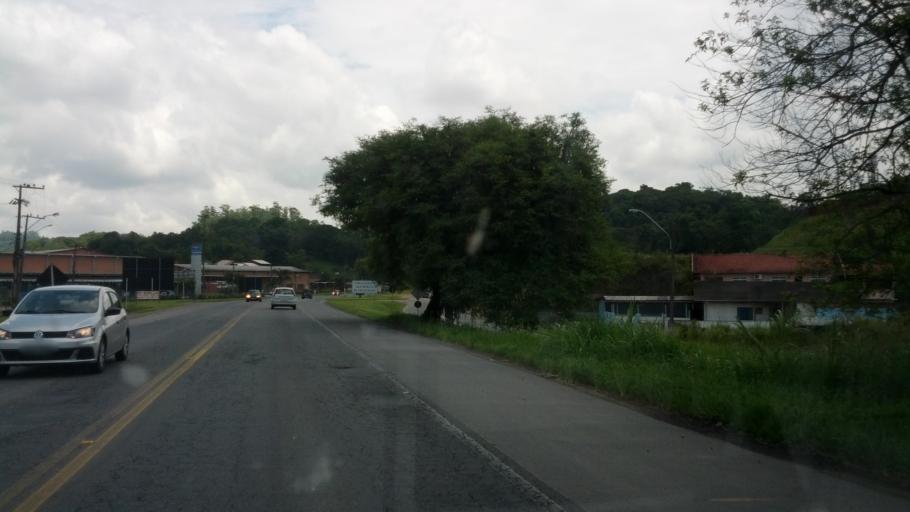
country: BR
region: Santa Catarina
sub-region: Blumenau
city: Blumenau
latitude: -26.8838
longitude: -49.1454
